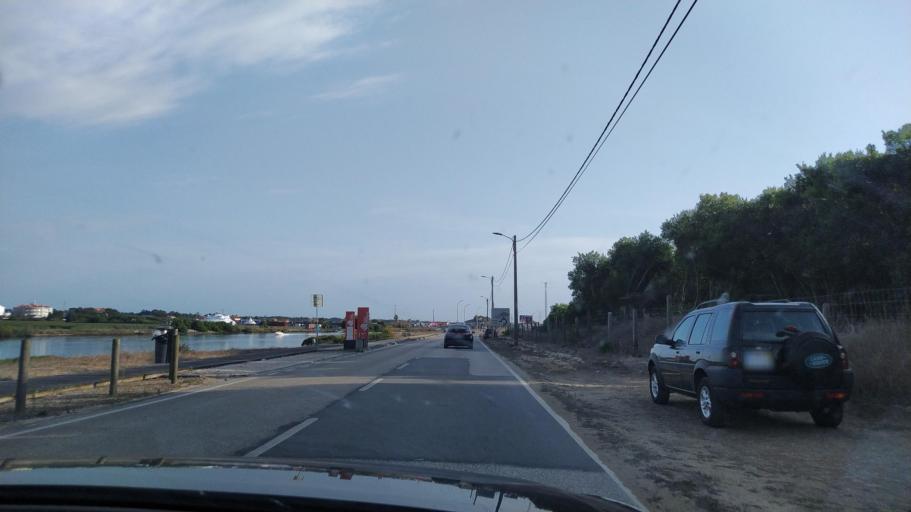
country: PT
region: Aveiro
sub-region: Ilhavo
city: Gafanha da Encarnacao
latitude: 40.5651
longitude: -8.7571
